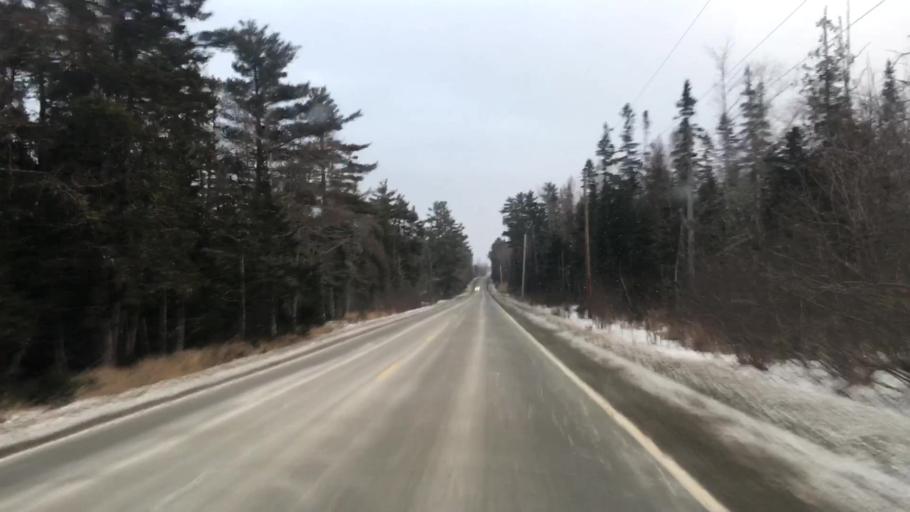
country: US
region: Maine
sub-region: Hancock County
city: Ellsworth
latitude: 44.6769
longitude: -68.3530
